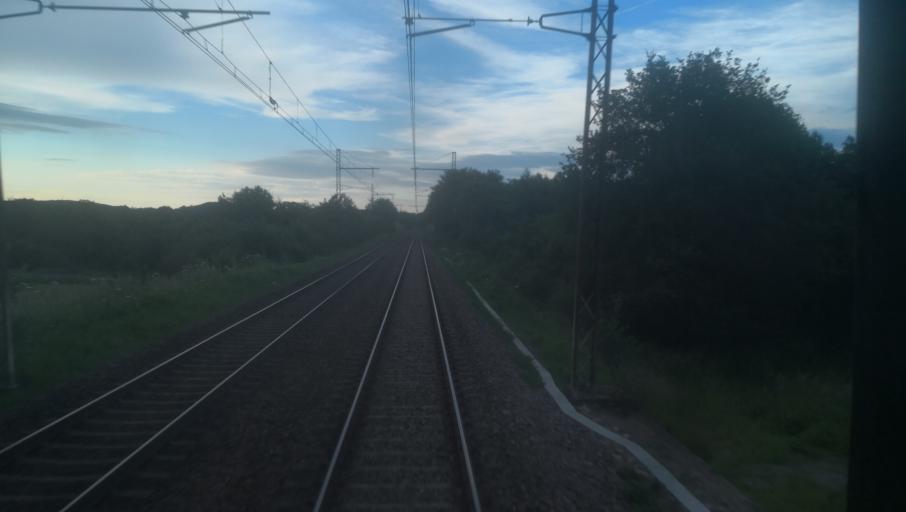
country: FR
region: Limousin
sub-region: Departement de la Creuse
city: La Souterraine
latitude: 46.2015
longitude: 1.4758
